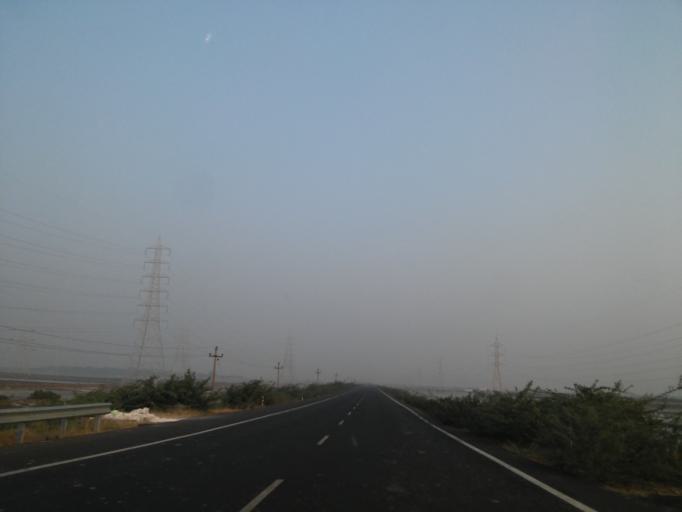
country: IN
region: Gujarat
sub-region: Kachchh
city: Rapar
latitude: 23.2057
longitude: 70.7144
